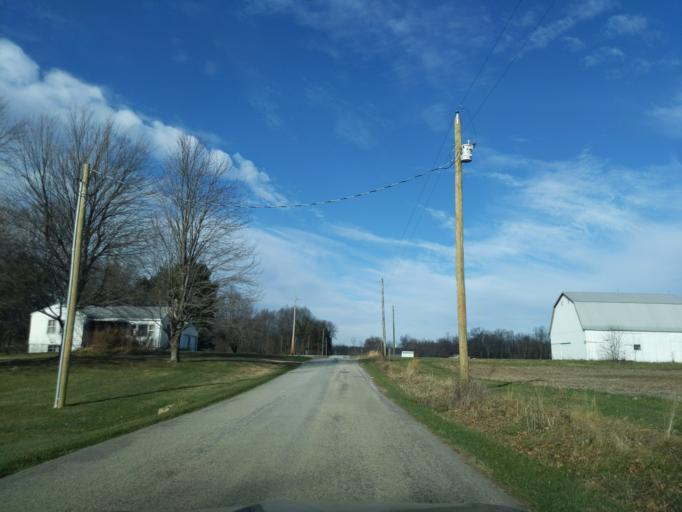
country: US
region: Indiana
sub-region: Decatur County
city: Greensburg
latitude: 39.2861
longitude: -85.4235
